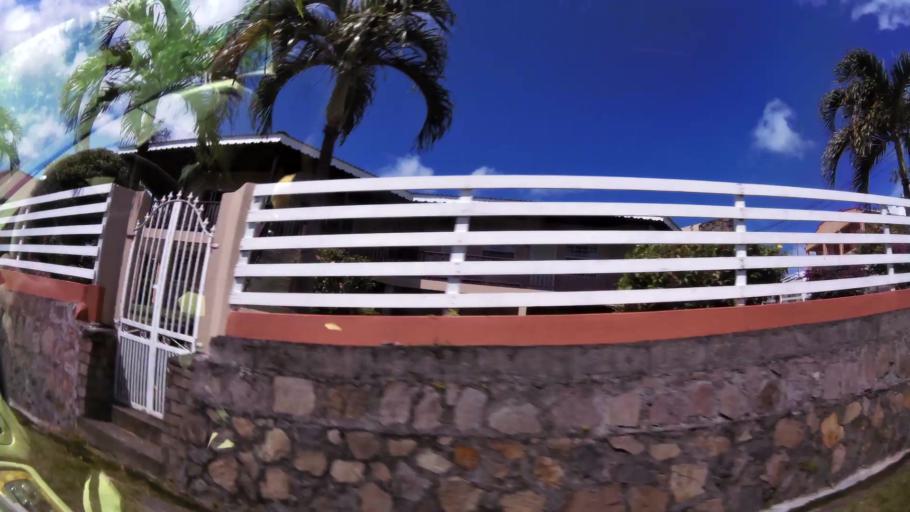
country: VC
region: Saint George
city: Kingstown
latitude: 13.1404
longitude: -61.2238
